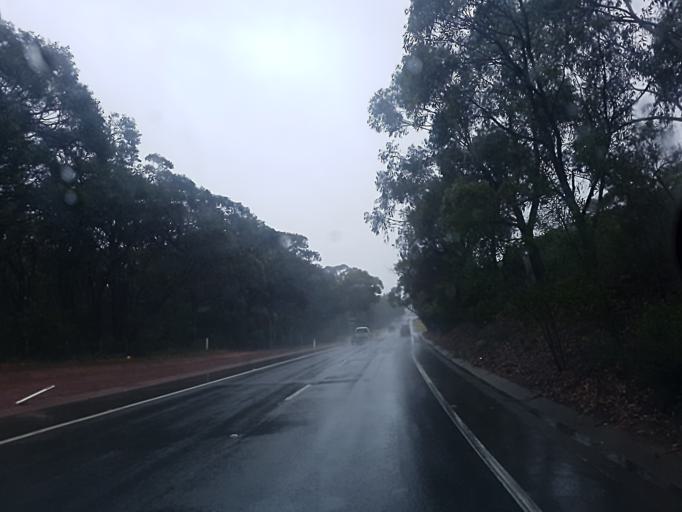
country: AU
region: New South Wales
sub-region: Warringah
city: Davidson
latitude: -33.7036
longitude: 151.2066
